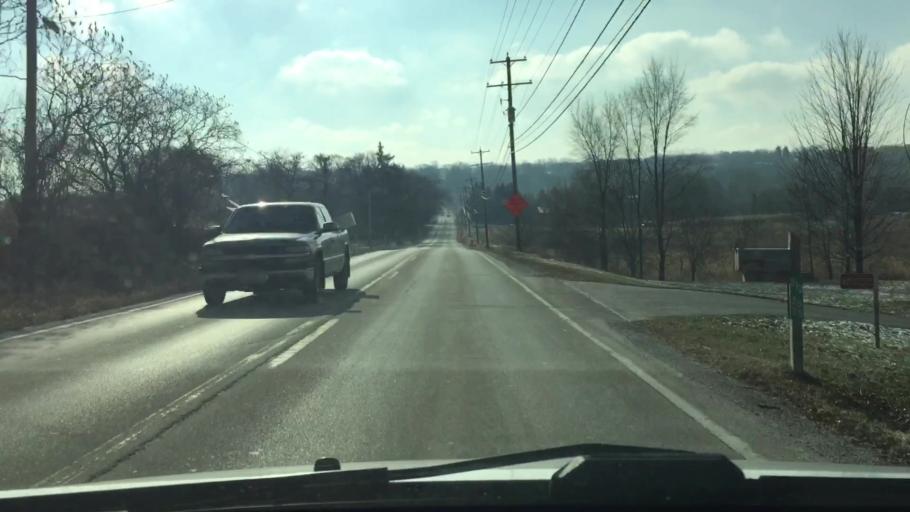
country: US
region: Wisconsin
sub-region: Waukesha County
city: Waukesha
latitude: 42.9991
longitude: -88.2904
